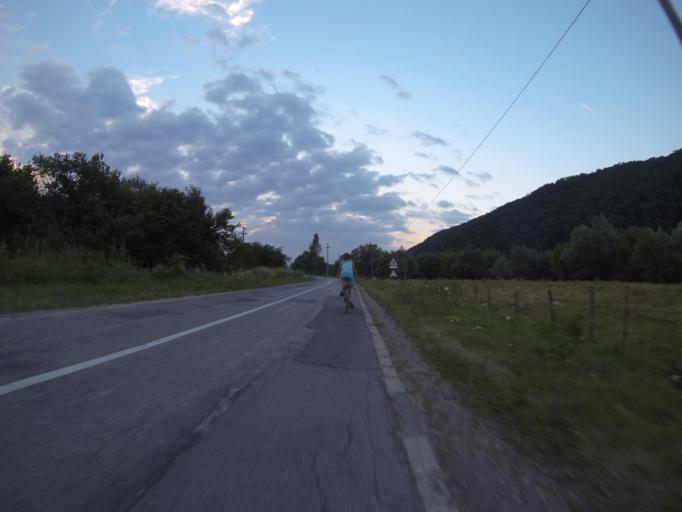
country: RO
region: Brasov
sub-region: Comuna Sinca Noua
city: Sinca Noua
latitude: 45.7372
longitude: 25.2285
